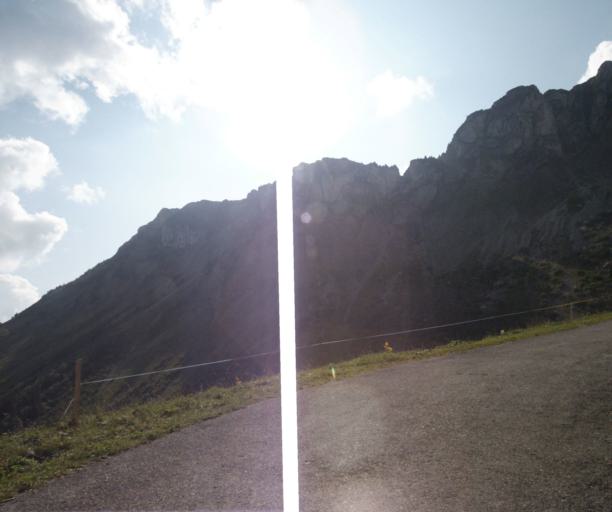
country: CH
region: Vaud
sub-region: Riviera-Pays-d'Enhaut District
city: Caux
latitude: 46.4250
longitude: 7.0018
